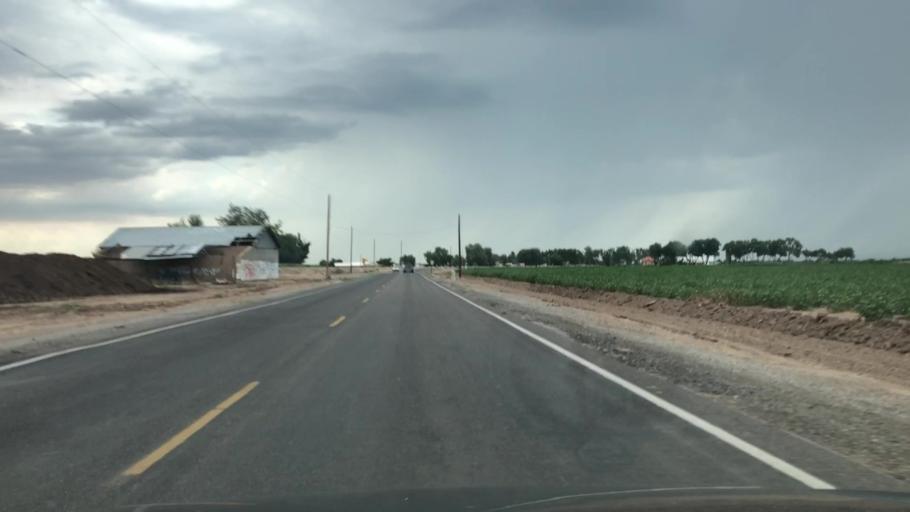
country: US
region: New Mexico
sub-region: Dona Ana County
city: Anthony
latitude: 32.0231
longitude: -106.6708
